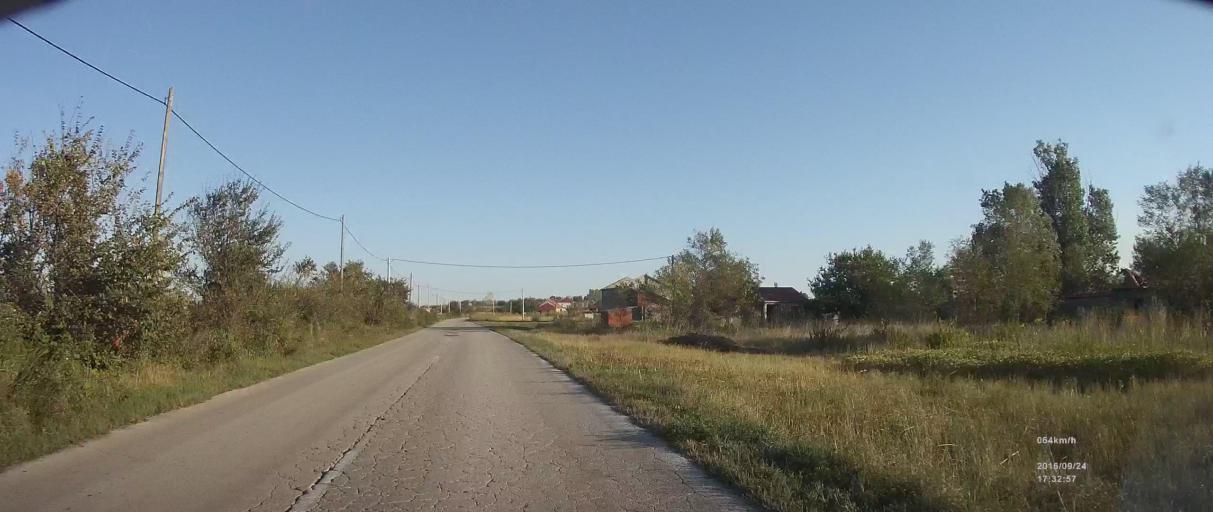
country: HR
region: Zadarska
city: Posedarje
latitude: 44.1783
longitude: 15.4540
